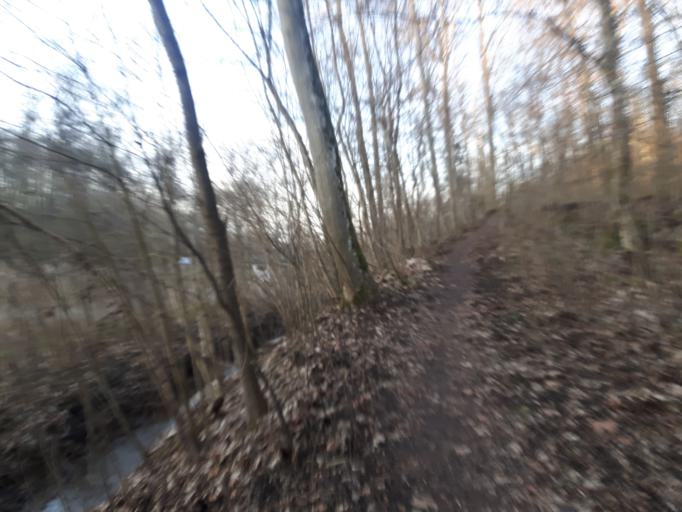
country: DE
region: Baden-Wuerttemberg
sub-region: Regierungsbezirk Stuttgart
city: Heilbronn
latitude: 49.1268
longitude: 9.2556
